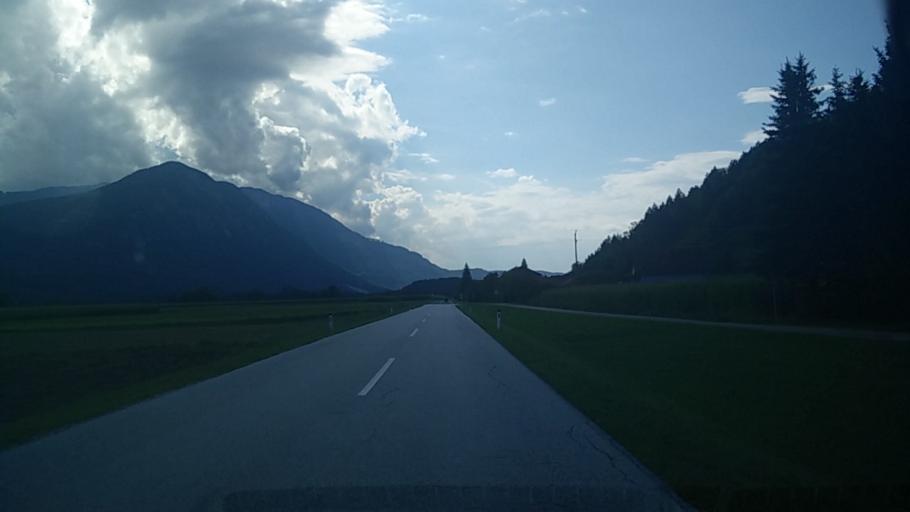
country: AT
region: Carinthia
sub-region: Politischer Bezirk Volkermarkt
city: Sittersdorf
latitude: 46.5473
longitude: 14.5995
